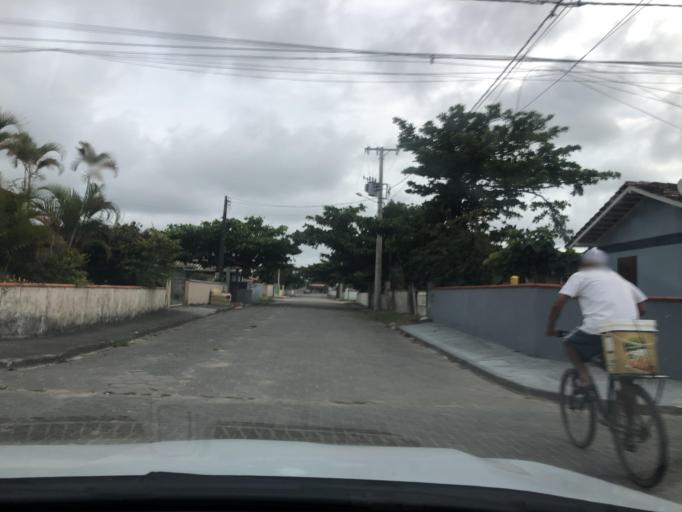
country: BR
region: Santa Catarina
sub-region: Sao Francisco Do Sul
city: Sao Francisco do Sul
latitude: -26.2276
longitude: -48.5195
